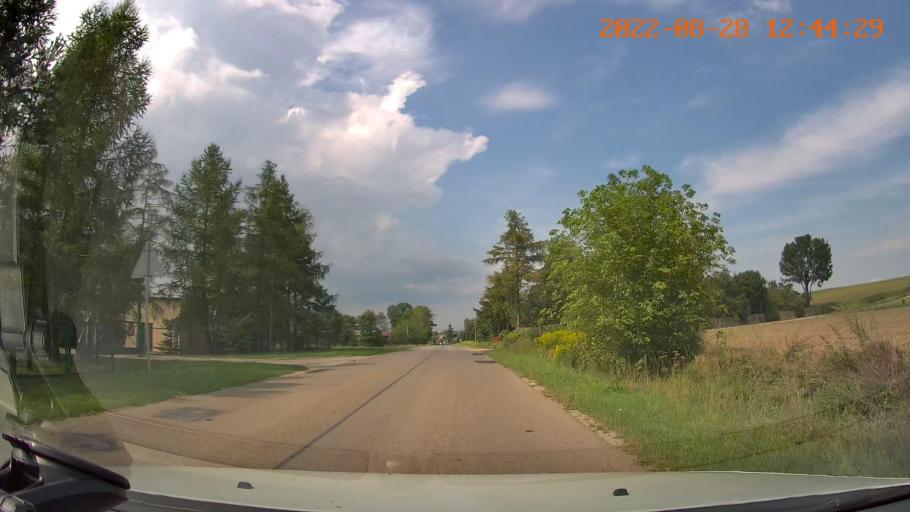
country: PL
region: Swietokrzyskie
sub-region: Powiat pinczowski
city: Dzialoszyce
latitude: 50.3739
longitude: 20.3175
